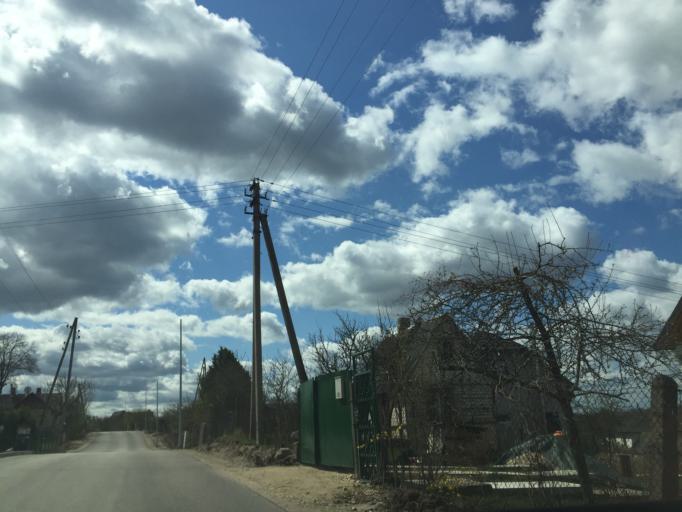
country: LV
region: Rezekne
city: Rezekne
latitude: 56.4880
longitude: 27.3238
